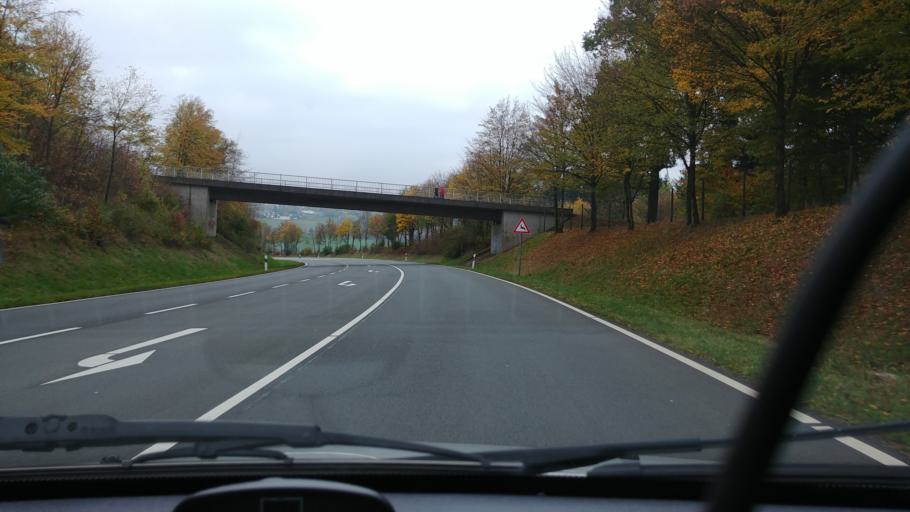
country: DE
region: Rheinland-Pfalz
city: Streithausen
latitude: 50.6834
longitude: 7.8146
